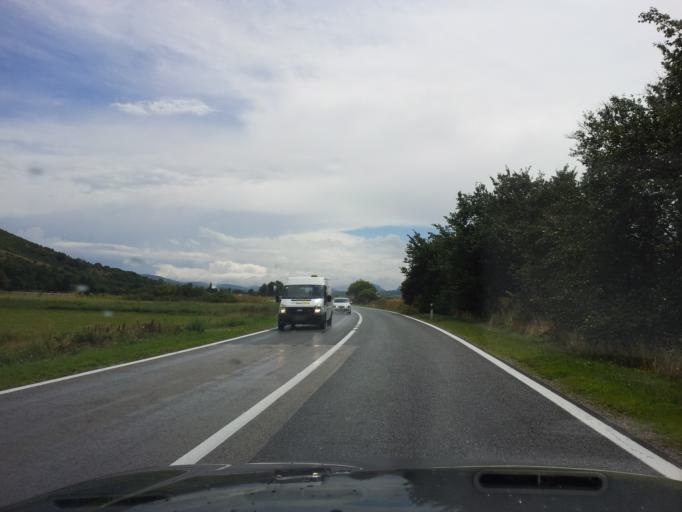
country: BA
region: Federation of Bosnia and Herzegovina
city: Bihac
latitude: 44.5983
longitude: 15.7346
